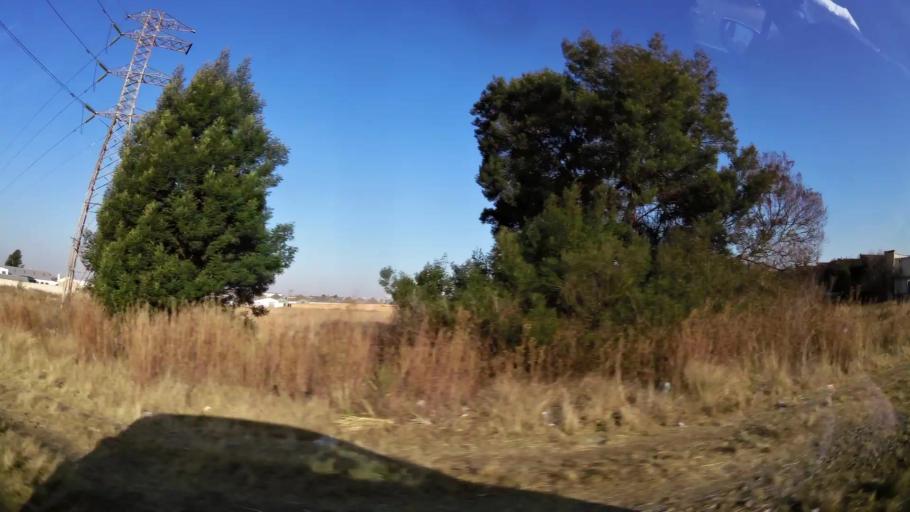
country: ZA
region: Gauteng
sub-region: West Rand District Municipality
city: Randfontein
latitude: -26.1927
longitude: 27.6846
